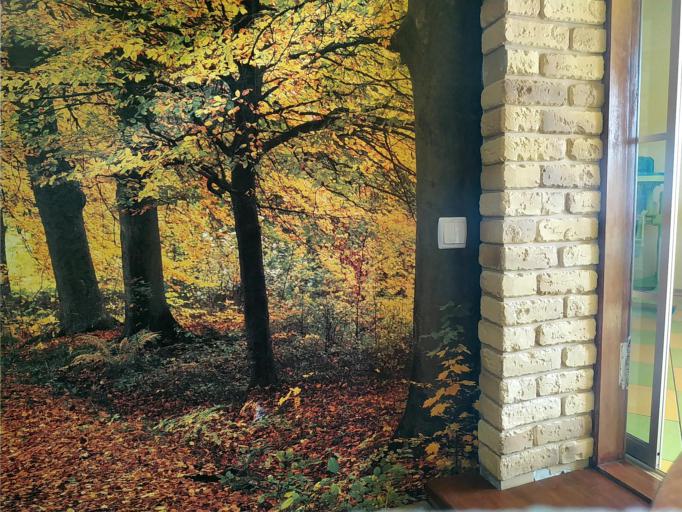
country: RU
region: Smolensk
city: Katyn'
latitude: 55.0036
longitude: 31.7682
